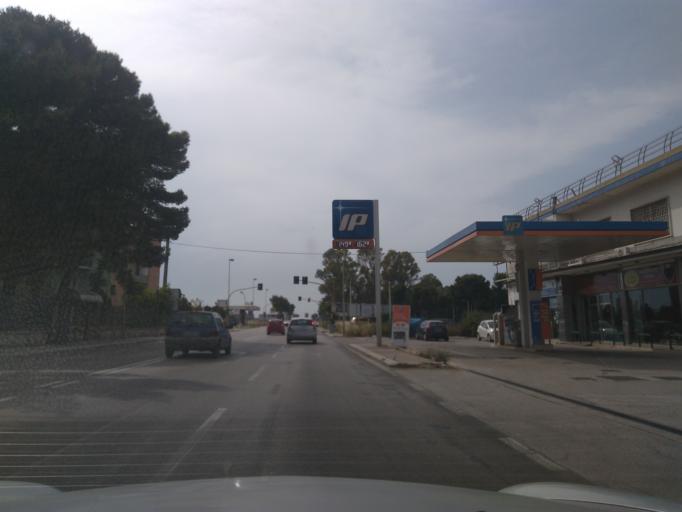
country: IT
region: Apulia
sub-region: Provincia di Bari
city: Bari
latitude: 41.1297
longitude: 16.8331
